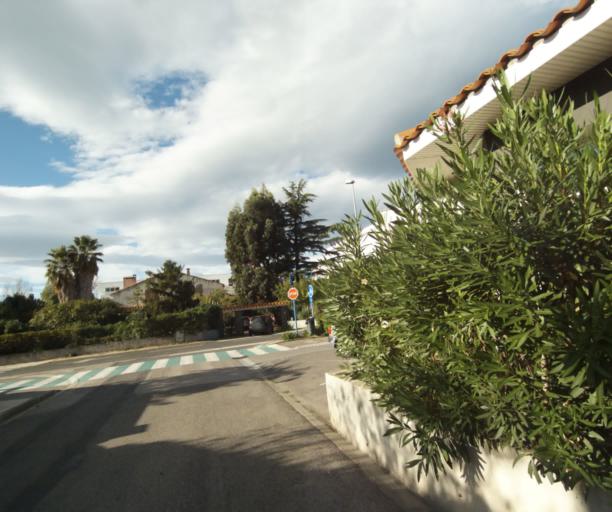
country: FR
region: Languedoc-Roussillon
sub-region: Departement des Pyrenees-Orientales
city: Argelers
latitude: 42.5475
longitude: 3.0356
